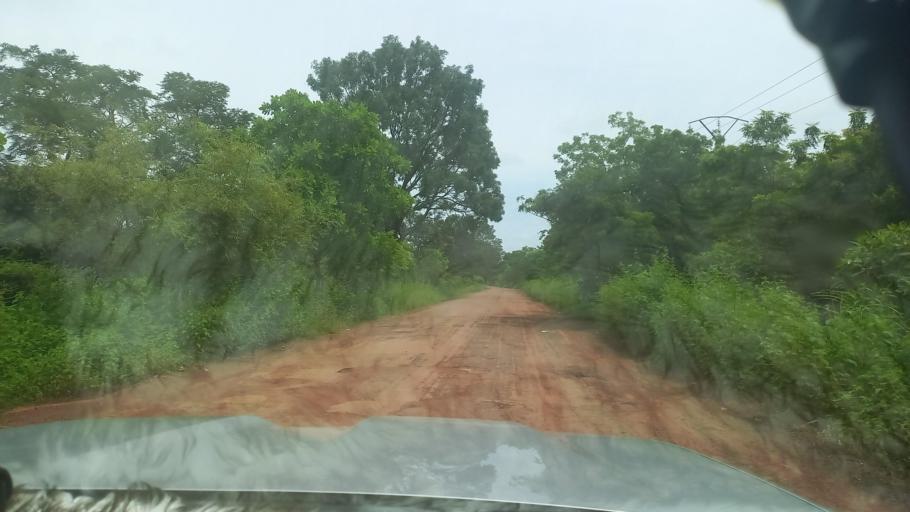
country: SN
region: Kolda
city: Marsassoum
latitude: 12.9045
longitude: -16.0193
